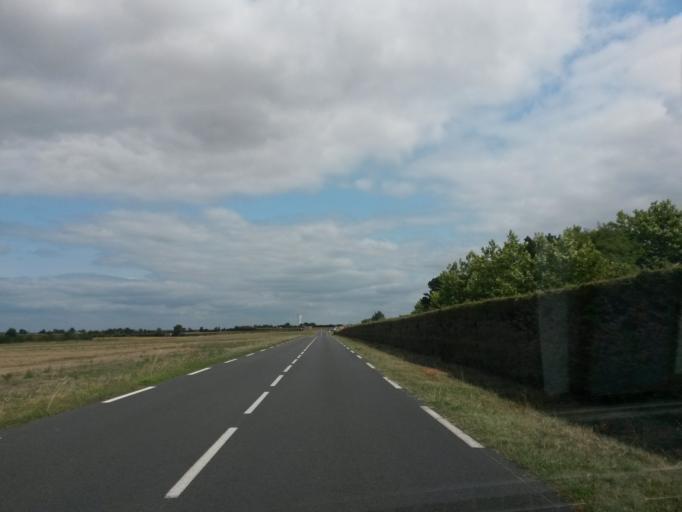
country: FR
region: Pays de la Loire
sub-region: Departement de la Vendee
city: Longeville-sur-Mer
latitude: 46.4188
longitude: -1.5307
